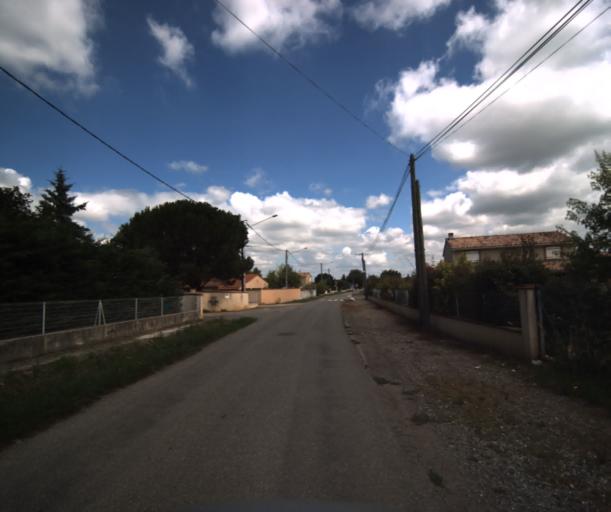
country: FR
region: Midi-Pyrenees
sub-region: Departement de la Haute-Garonne
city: Lacasse
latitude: 43.3885
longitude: 1.2587
